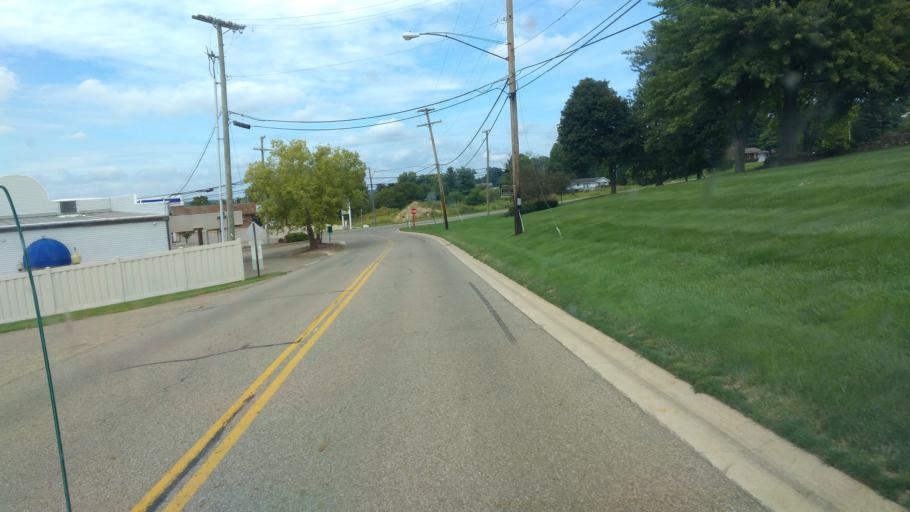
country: US
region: Ohio
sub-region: Holmes County
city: Millersburg
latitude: 40.5592
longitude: -81.8061
